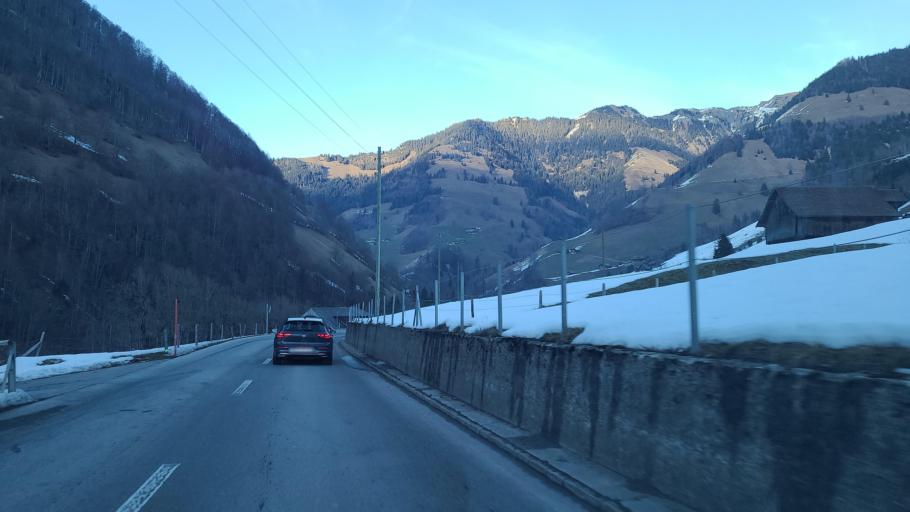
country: CH
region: Obwalden
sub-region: Obwalden
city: Kerns
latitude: 46.8398
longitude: 8.2932
